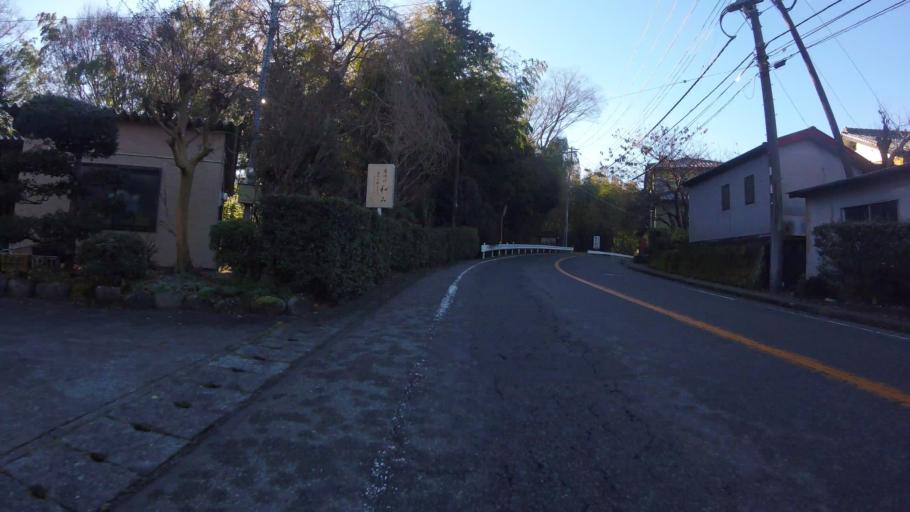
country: JP
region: Shizuoka
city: Heda
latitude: 34.9058
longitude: 138.9246
